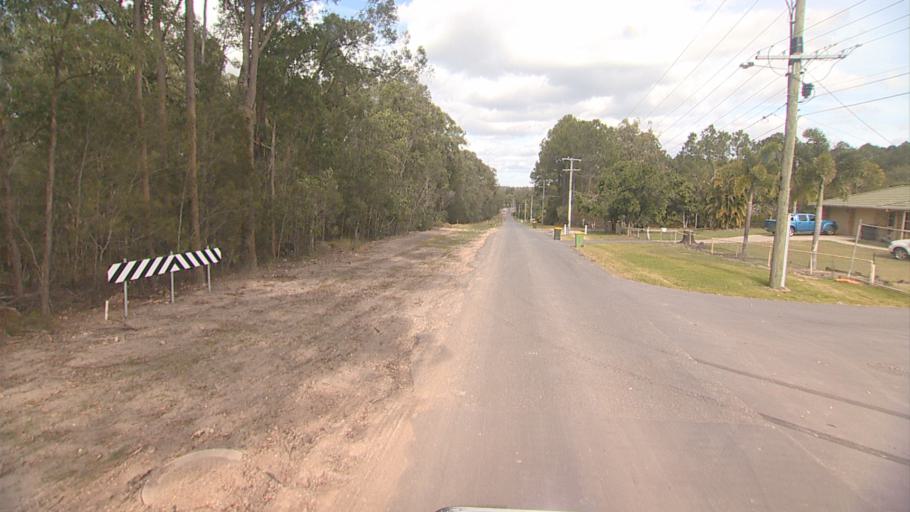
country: AU
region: Queensland
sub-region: Logan
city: Woodridge
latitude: -27.6606
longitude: 153.0673
